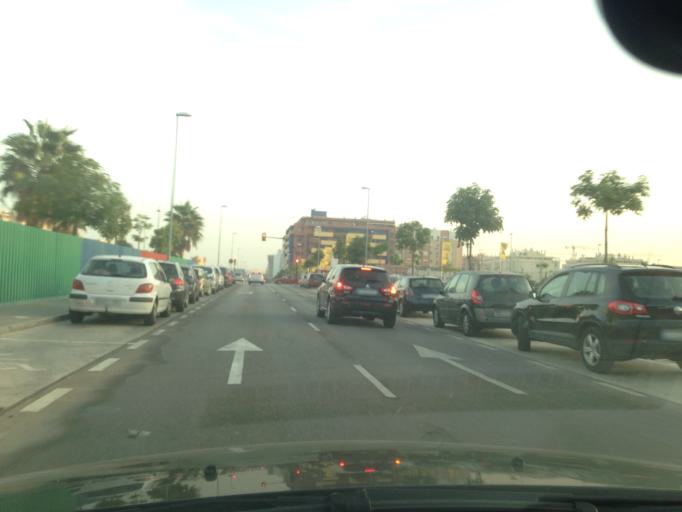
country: ES
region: Andalusia
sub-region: Provincia de Malaga
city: Malaga
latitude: 36.7248
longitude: -4.4630
